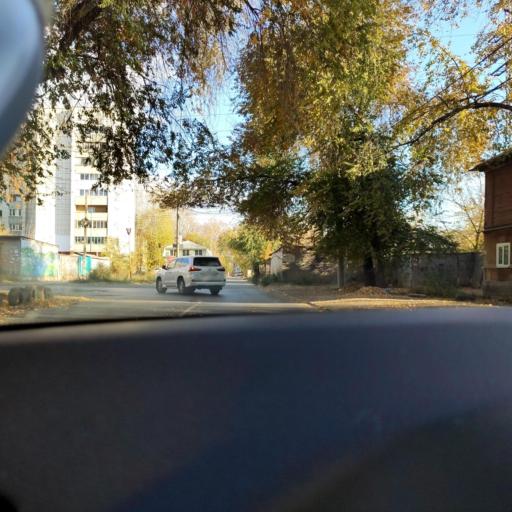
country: RU
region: Samara
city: Petra-Dubrava
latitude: 53.2344
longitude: 50.2844
